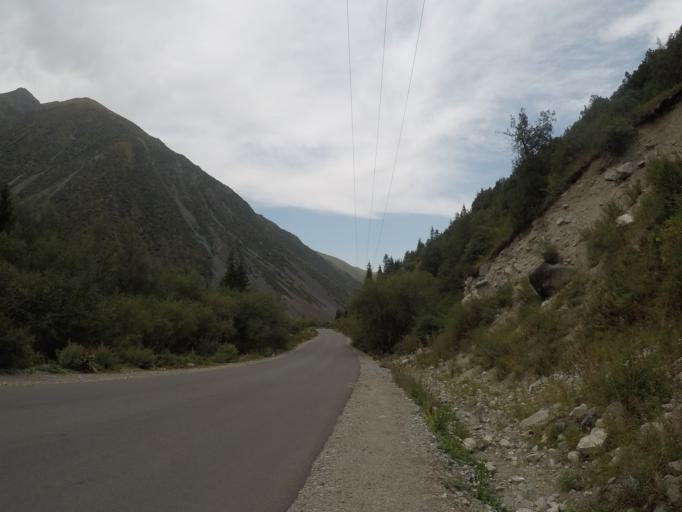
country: KG
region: Chuy
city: Bishkek
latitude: 42.5739
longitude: 74.4830
